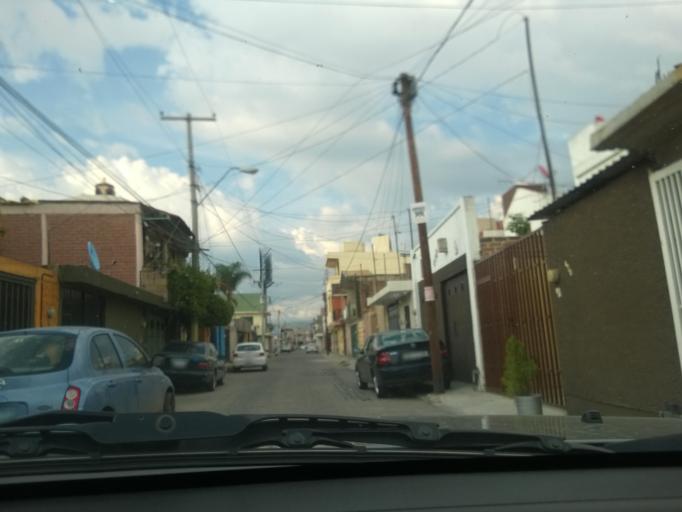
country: MX
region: Guanajuato
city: Leon
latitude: 21.1276
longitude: -101.6497
